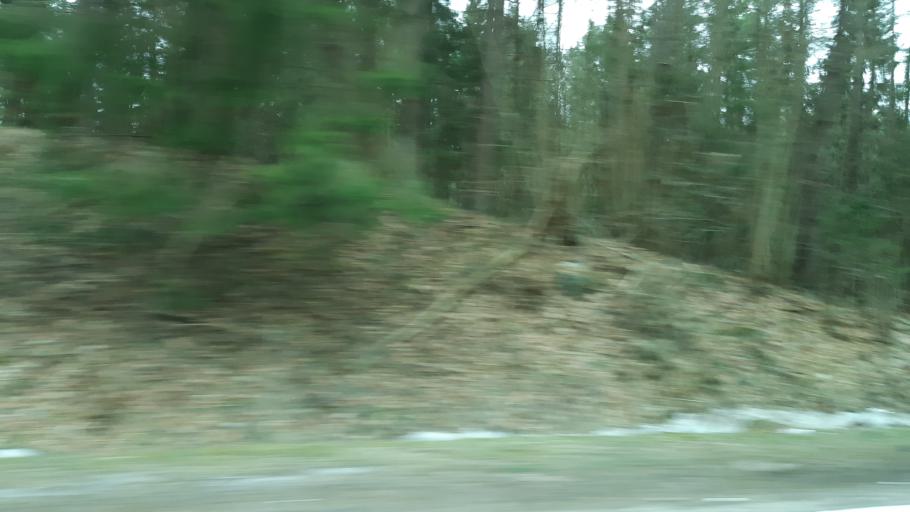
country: PL
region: Podlasie
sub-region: Suwalki
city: Suwalki
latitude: 54.2872
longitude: 22.9536
